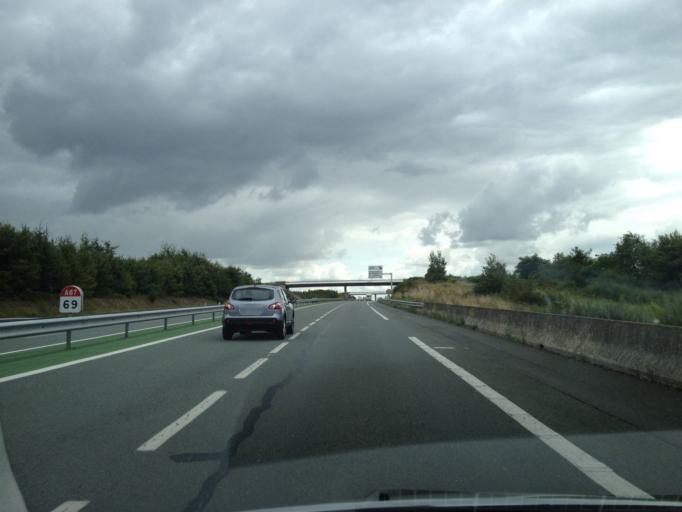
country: FR
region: Pays de la Loire
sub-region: Departement de la Vendee
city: Chambretaud
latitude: 46.9402
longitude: -0.9797
